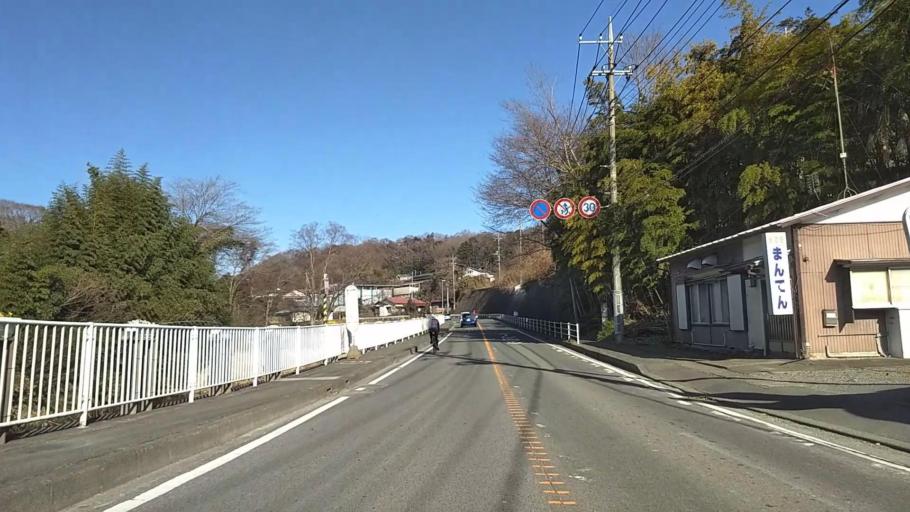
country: JP
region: Kanagawa
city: Atsugi
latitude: 35.4722
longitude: 139.3112
